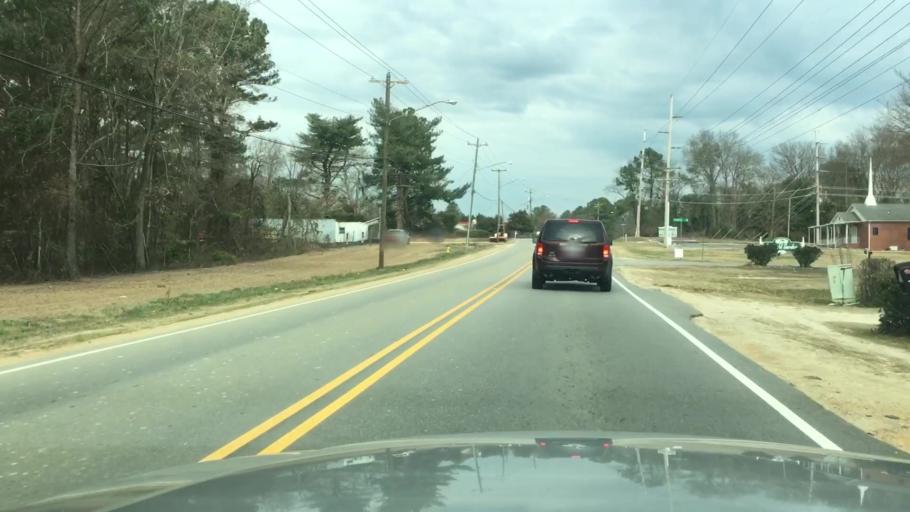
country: US
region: North Carolina
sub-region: Hoke County
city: Rockfish
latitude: 35.0226
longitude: -79.0024
